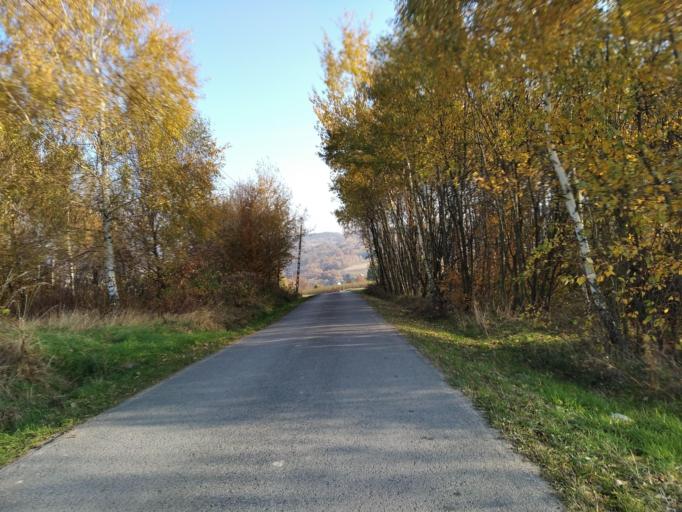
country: PL
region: Subcarpathian Voivodeship
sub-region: Powiat strzyzowski
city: Babica
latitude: 49.9032
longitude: 21.8574
